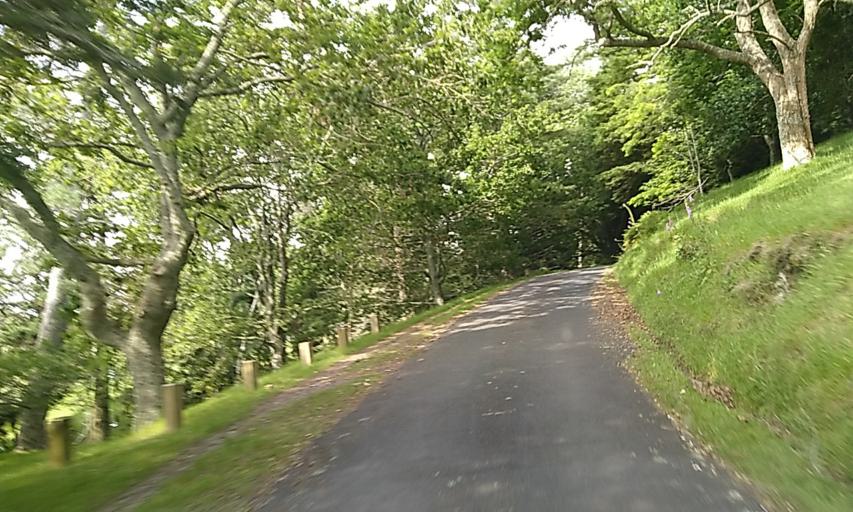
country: NZ
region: Bay of Plenty
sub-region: Tauranga City
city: Tauranga
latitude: -37.8145
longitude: 176.0417
